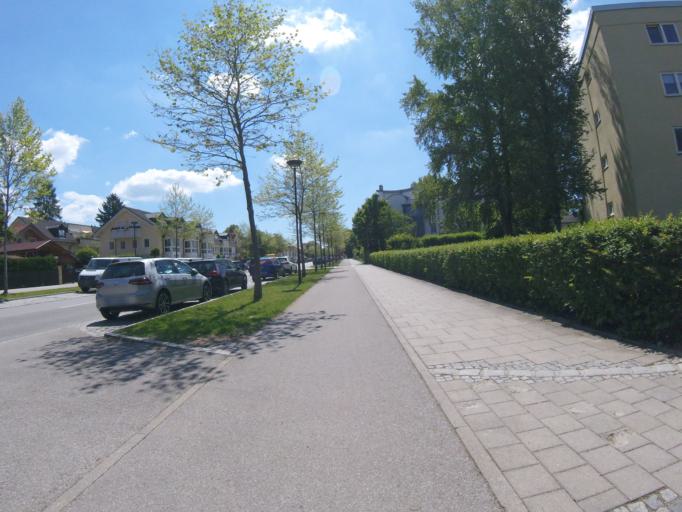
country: DE
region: Bavaria
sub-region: Upper Bavaria
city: Neubiberg
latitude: 48.0700
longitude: 11.6569
